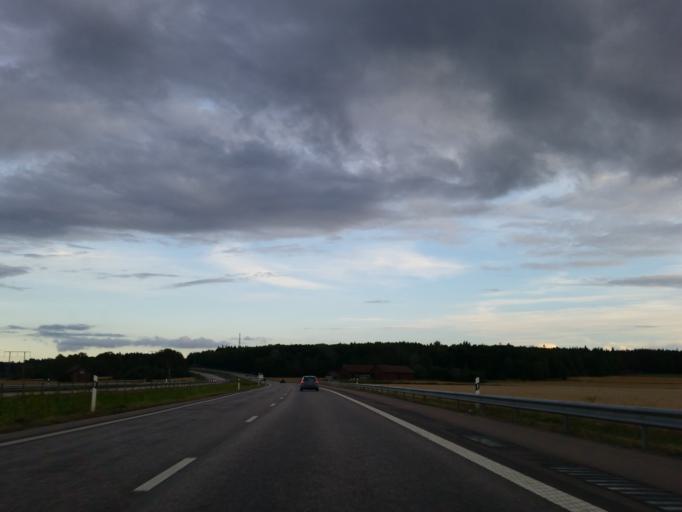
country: SE
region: Uppsala
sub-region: Uppsala Kommun
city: Saevja
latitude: 59.8100
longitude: 17.7573
